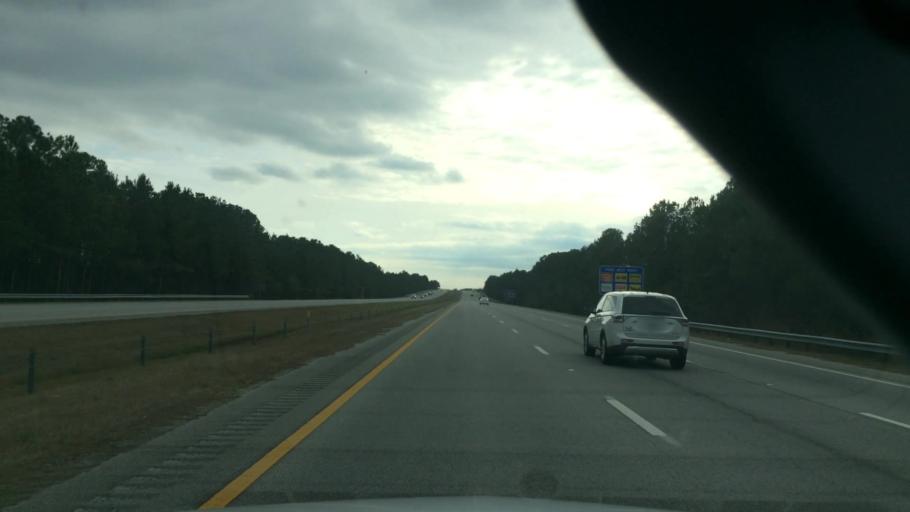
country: US
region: South Carolina
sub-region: Horry County
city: North Myrtle Beach
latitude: 33.8596
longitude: -78.6960
